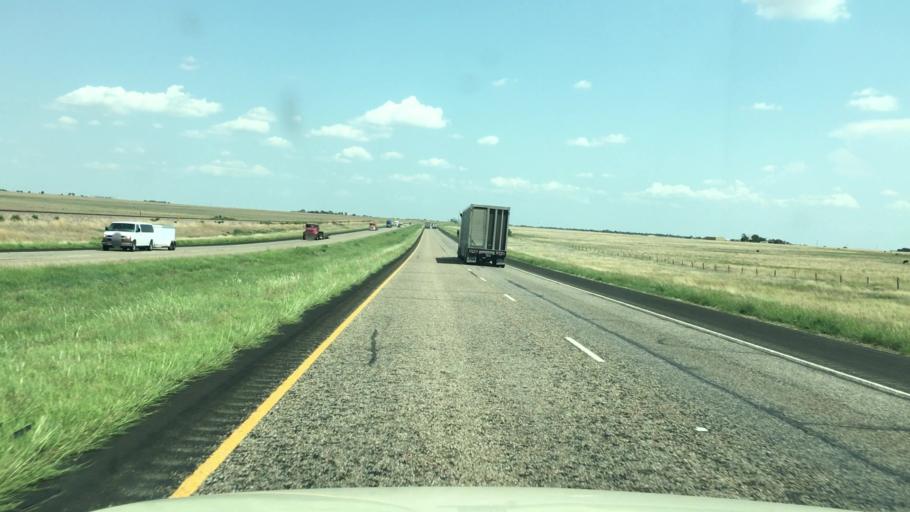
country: US
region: Texas
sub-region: Armstrong County
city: Claude
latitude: 35.1294
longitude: -101.4101
